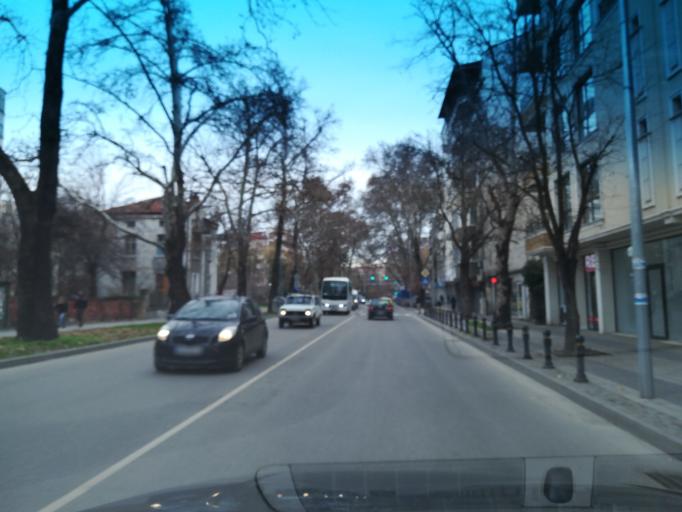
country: BG
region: Plovdiv
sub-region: Obshtina Plovdiv
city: Plovdiv
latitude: 42.1445
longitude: 24.7320
